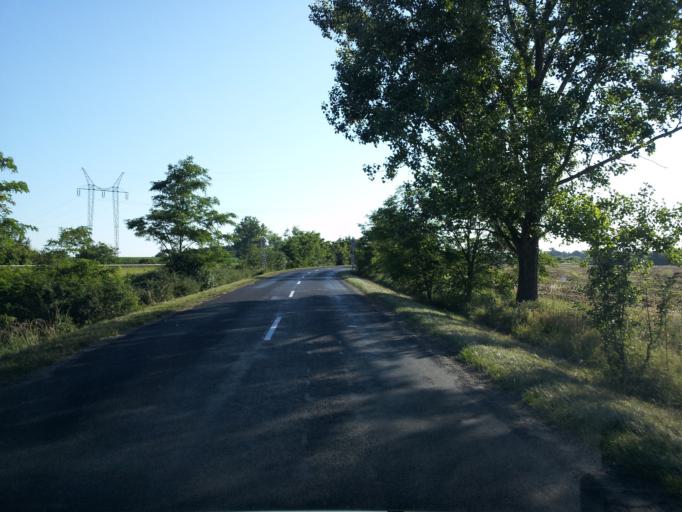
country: HU
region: Fejer
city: Lepseny
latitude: 47.0453
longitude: 18.2375
